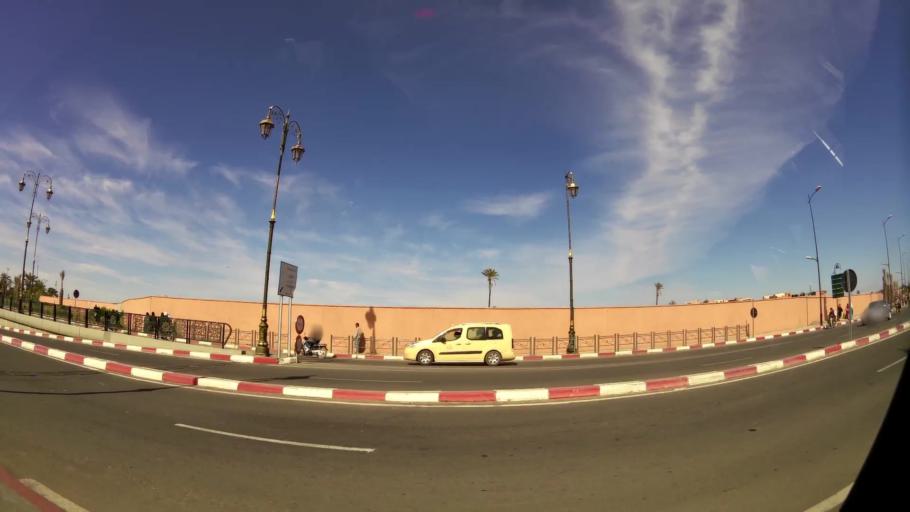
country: MA
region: Marrakech-Tensift-Al Haouz
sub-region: Marrakech
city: Marrakesh
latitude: 31.6431
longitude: -7.9868
